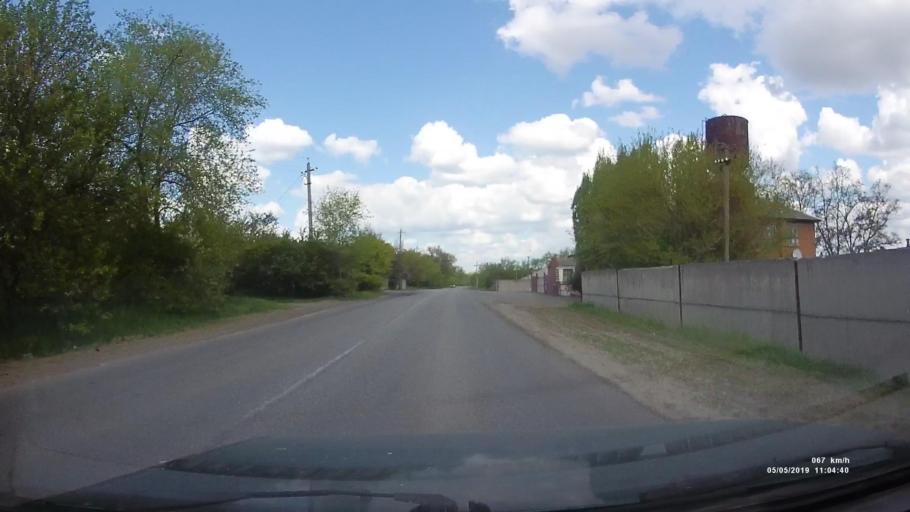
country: RU
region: Rostov
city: Ust'-Donetskiy
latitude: 47.6991
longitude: 40.9159
